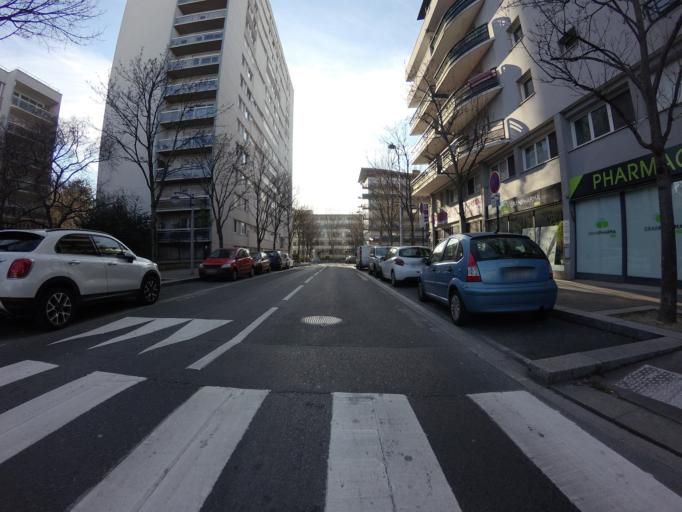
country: FR
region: Ile-de-France
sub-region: Departement des Hauts-de-Seine
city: Clichy
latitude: 48.9095
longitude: 2.3084
